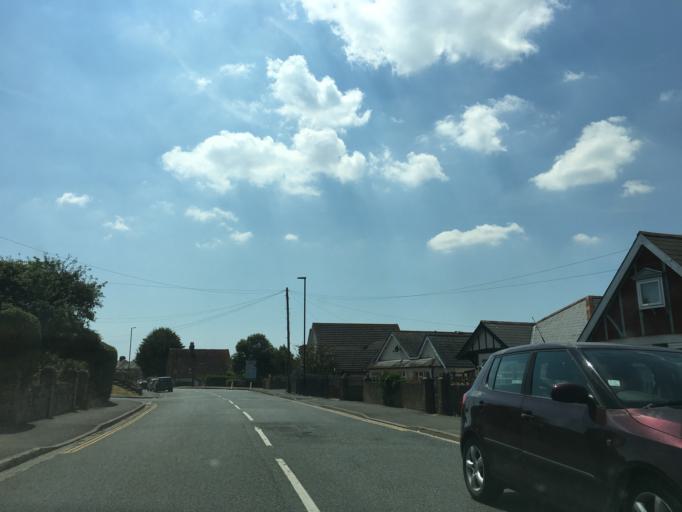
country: GB
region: England
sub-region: Isle of Wight
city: Ryde
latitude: 50.7196
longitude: -1.1536
